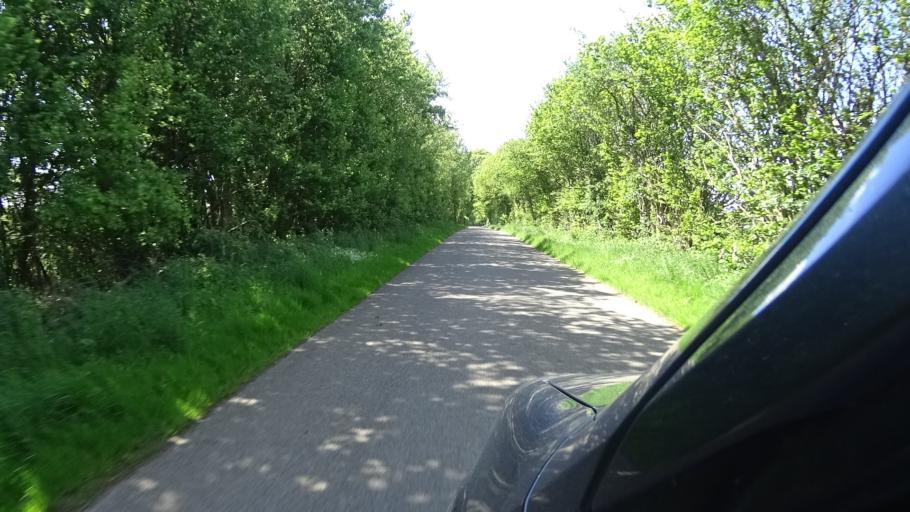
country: DK
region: South Denmark
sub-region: Vejle Kommune
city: Borkop
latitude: 55.6133
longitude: 9.6529
